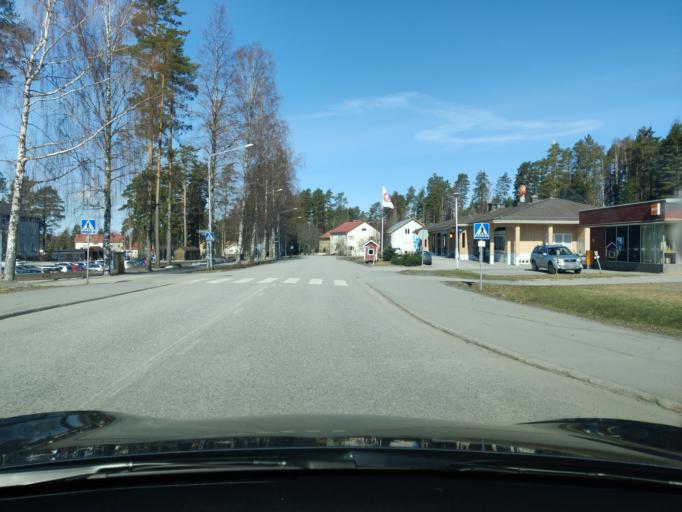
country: FI
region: Northern Savo
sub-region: Kuopio
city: Vehmersalmi
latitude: 62.7612
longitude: 28.0288
